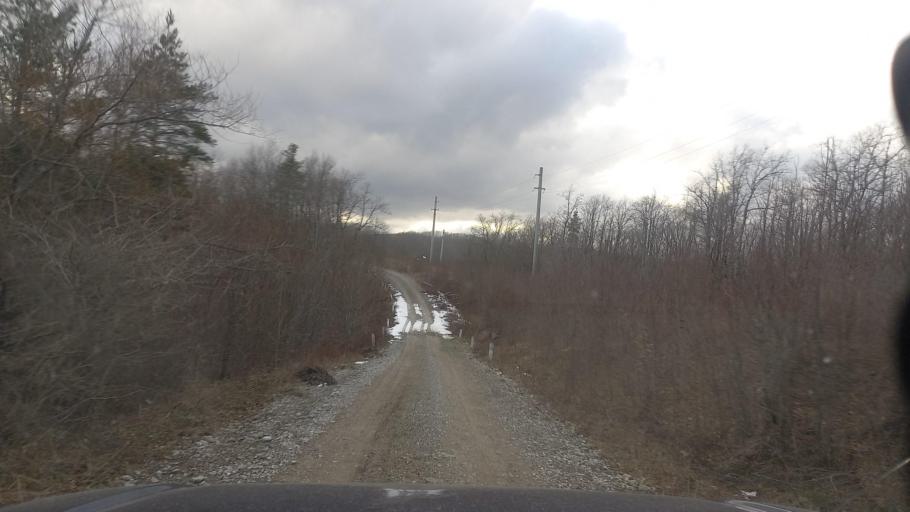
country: RU
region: Krasnodarskiy
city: Smolenskaya
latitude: 44.5736
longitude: 38.8002
